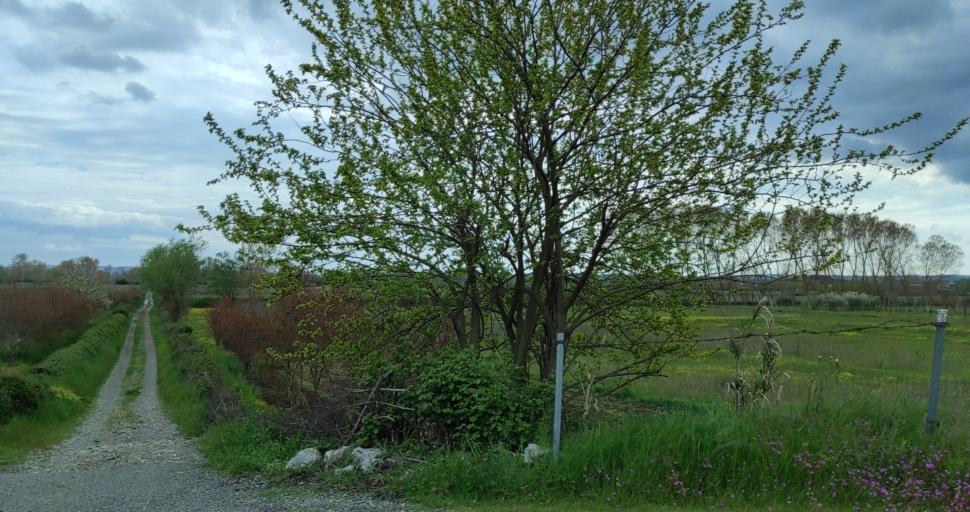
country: AL
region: Shkoder
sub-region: Rrethi i Shkodres
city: Dajc
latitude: 42.0147
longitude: 19.4016
